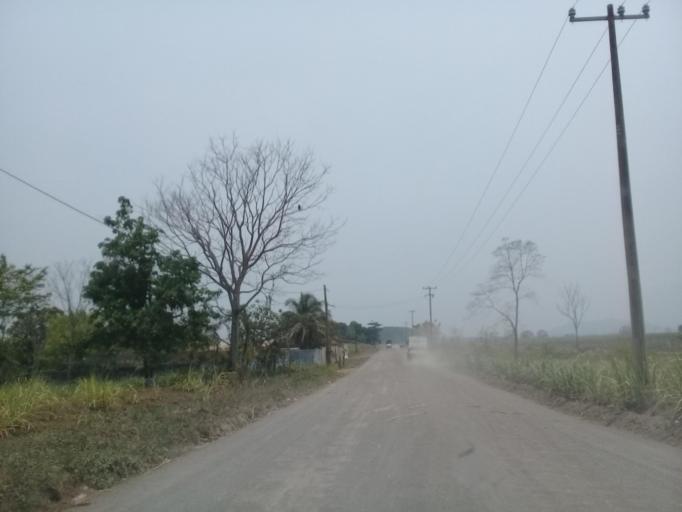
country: MX
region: Veracruz
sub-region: Tezonapa
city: Laguna Chica (Pueblo Nuevo)
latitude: 18.5384
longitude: -96.7389
